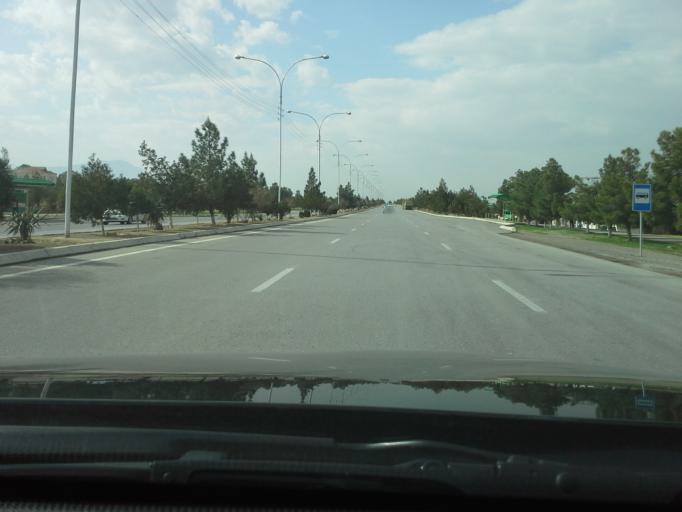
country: TM
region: Ahal
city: Ashgabat
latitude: 37.9652
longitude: 58.3070
